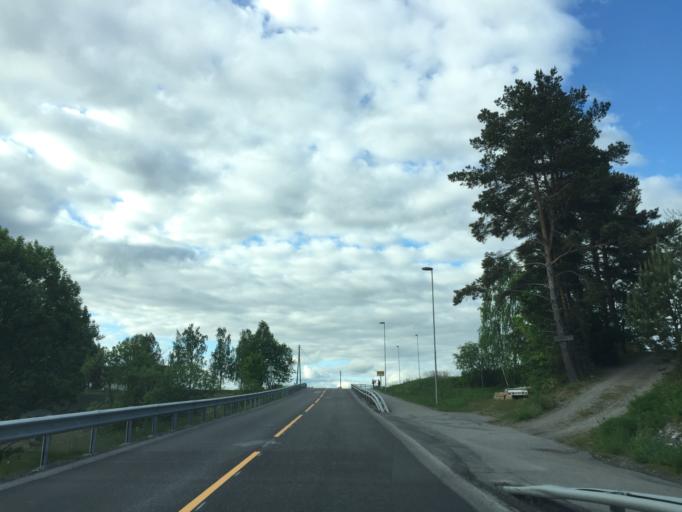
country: NO
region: Akershus
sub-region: Fet
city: Fetsund
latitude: 59.9353
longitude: 11.1885
